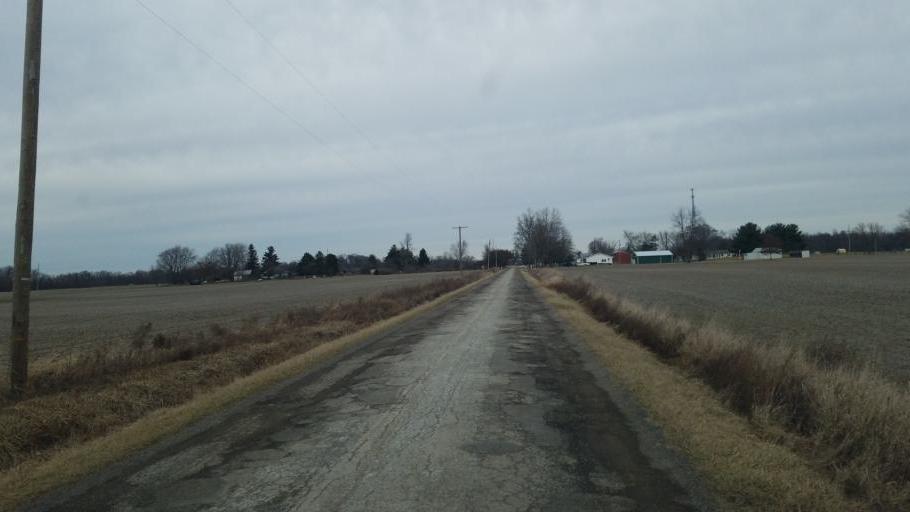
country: US
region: Ohio
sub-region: Morrow County
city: Cardington
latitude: 40.4649
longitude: -82.9305
